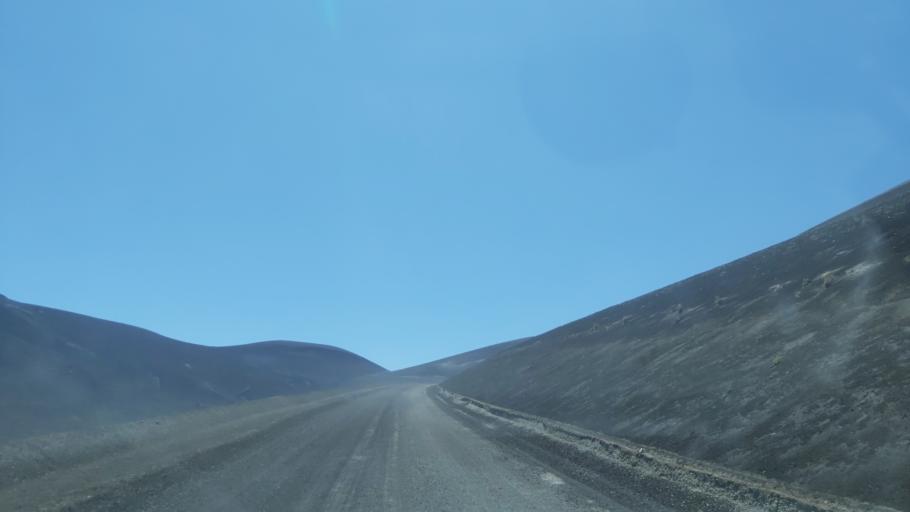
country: CL
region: Araucania
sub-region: Provincia de Cautin
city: Vilcun
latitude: -38.3996
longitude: -71.5452
